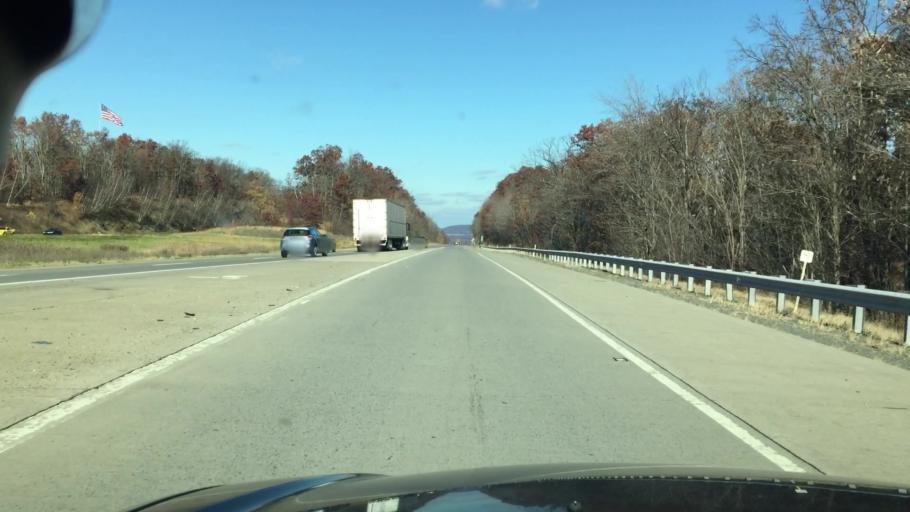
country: US
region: Pennsylvania
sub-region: Luzerne County
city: Freeland
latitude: 41.0844
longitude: -75.9627
